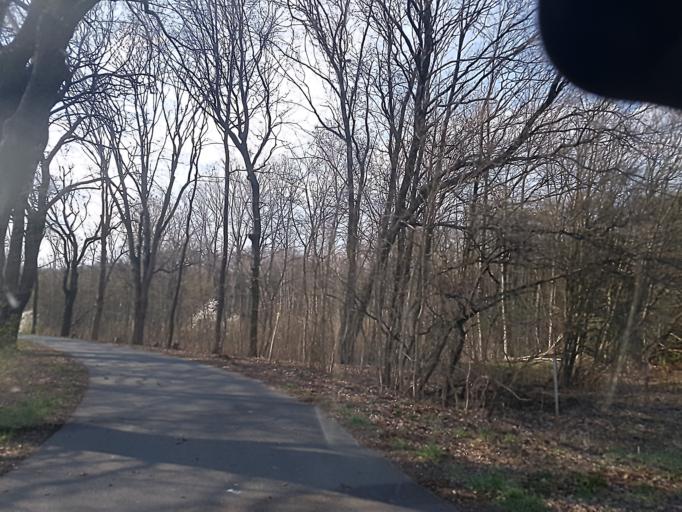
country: DE
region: Brandenburg
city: Doberlug-Kirchhain
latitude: 51.6104
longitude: 13.5357
